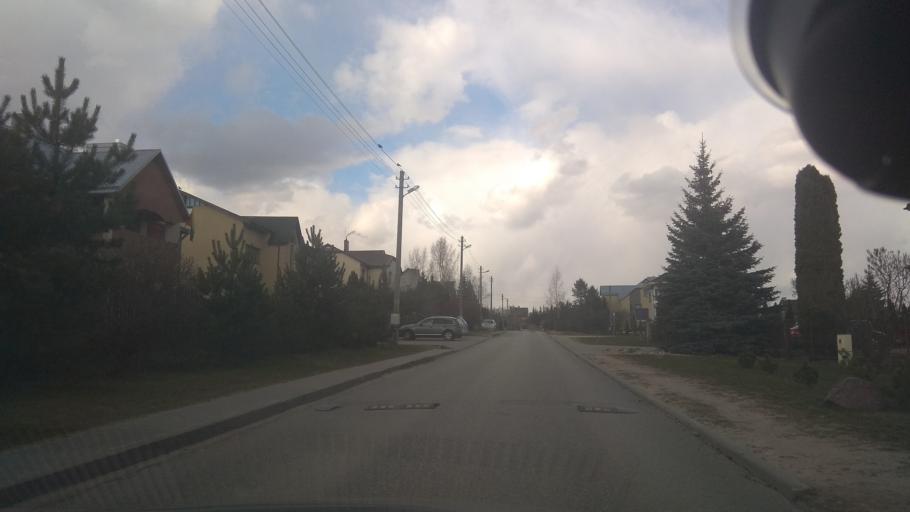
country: LT
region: Vilnius County
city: Pasilaiciai
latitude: 54.7368
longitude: 25.2020
